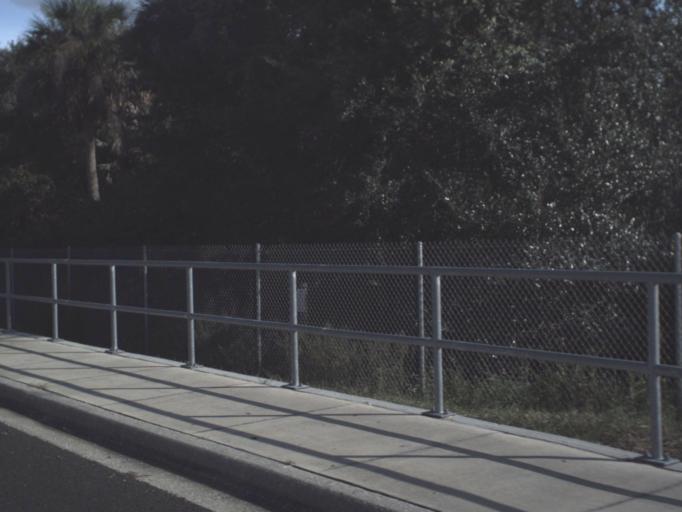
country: US
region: Florida
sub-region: Hillsborough County
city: Westchase
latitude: 28.0188
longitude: -82.6215
